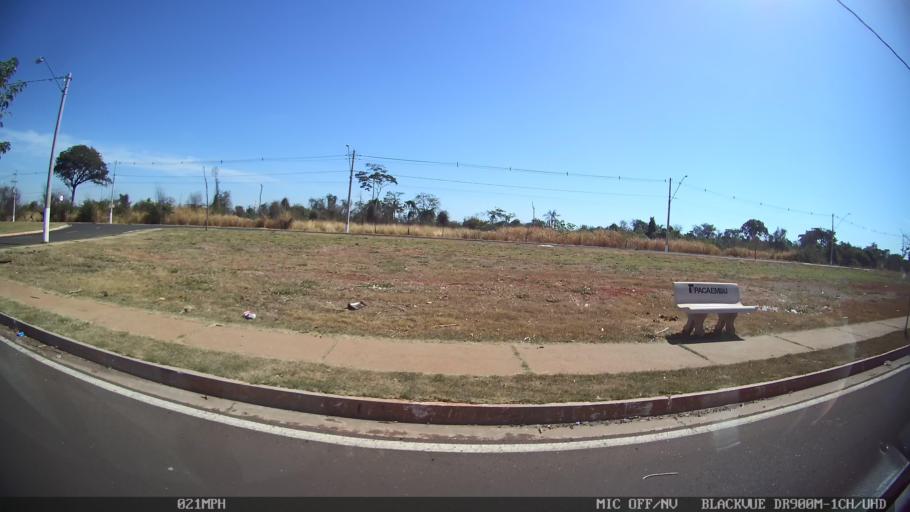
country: BR
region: Sao Paulo
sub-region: Sao Jose Do Rio Preto
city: Sao Jose do Rio Preto
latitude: -20.7478
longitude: -49.4370
